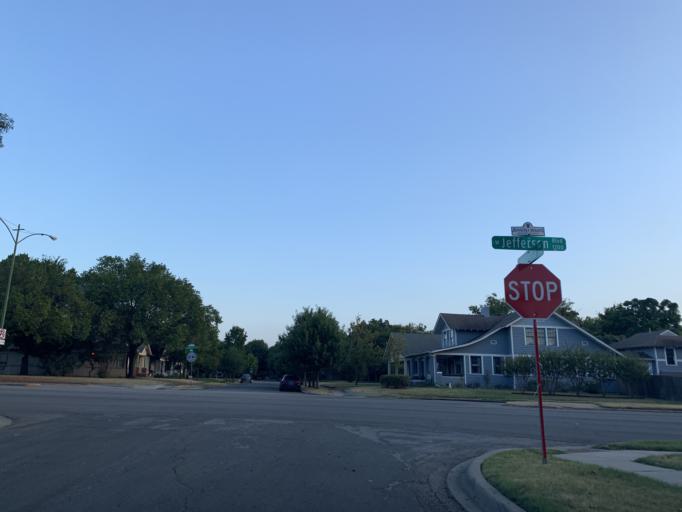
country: US
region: Texas
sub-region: Dallas County
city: Cockrell Hill
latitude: 32.7437
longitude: -96.8417
